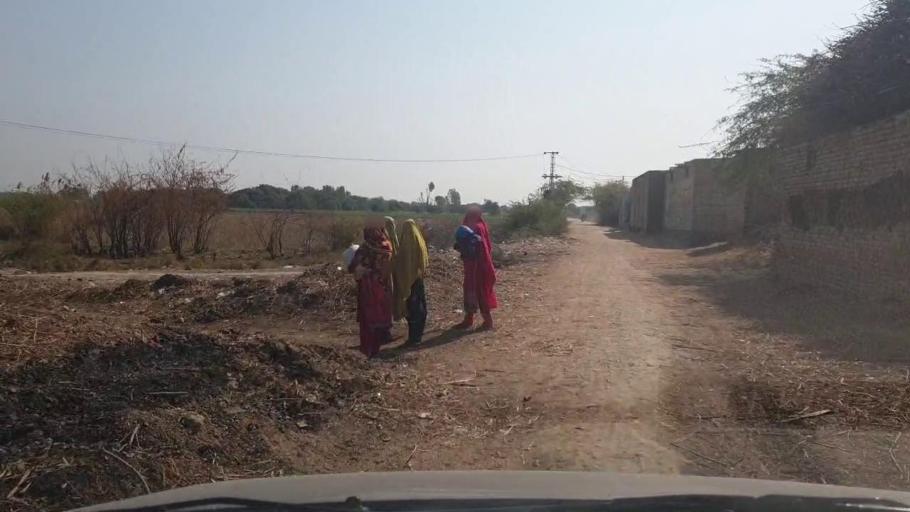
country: PK
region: Sindh
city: Mirwah Gorchani
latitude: 25.2520
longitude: 69.1206
